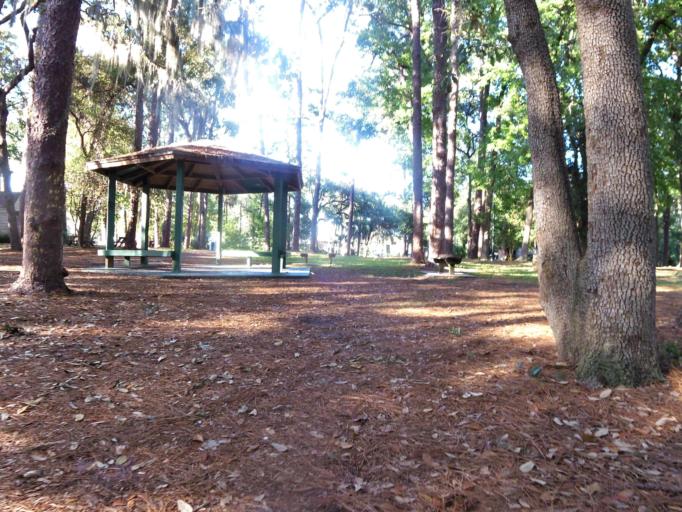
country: US
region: Florida
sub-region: Duval County
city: Jacksonville
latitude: 30.2972
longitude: -81.7108
